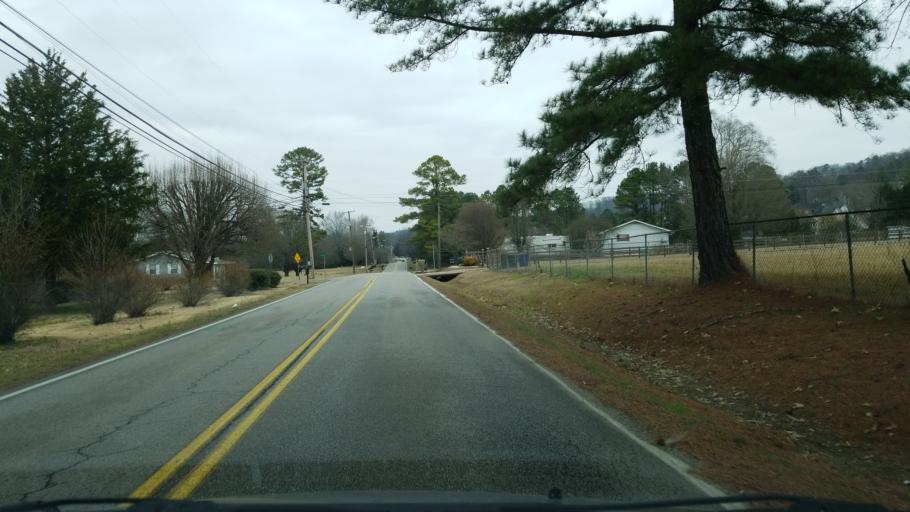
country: US
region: Tennessee
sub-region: Hamilton County
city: East Brainerd
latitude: 35.0053
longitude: -85.1303
